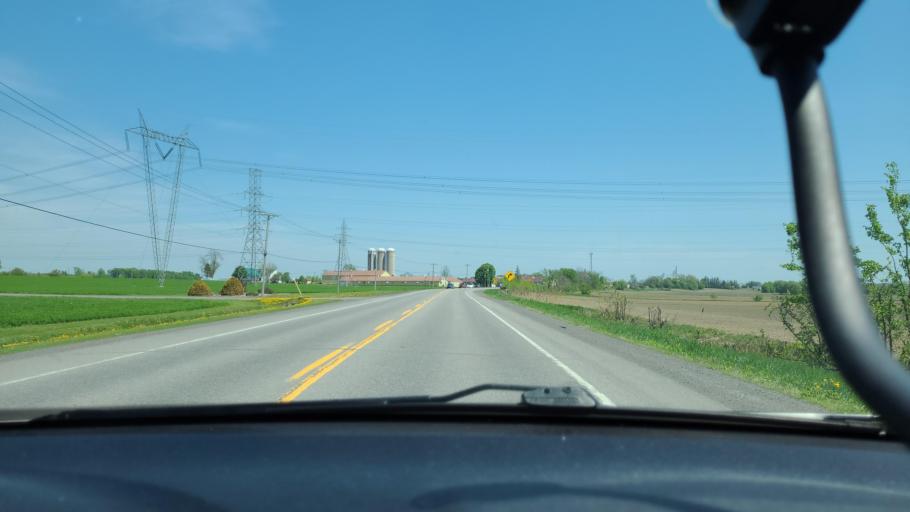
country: CA
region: Quebec
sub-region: Laurentides
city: Mirabel
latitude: 45.6011
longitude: -74.0483
